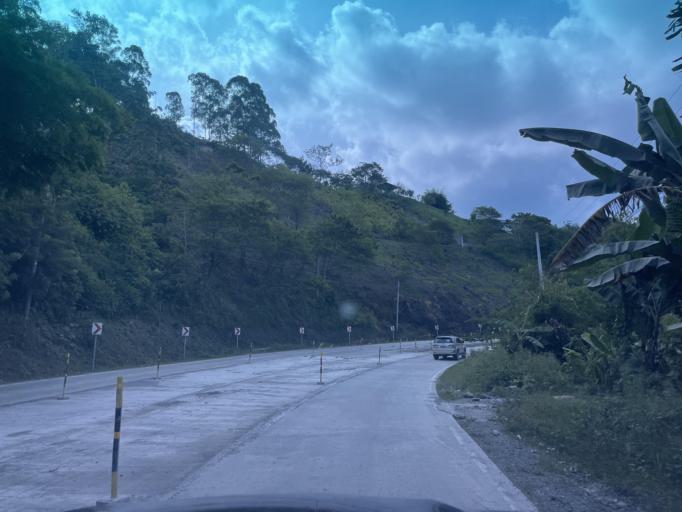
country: PH
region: Davao
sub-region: Province of Davao del Sur
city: Tamugan
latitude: 7.3330
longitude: 125.2936
